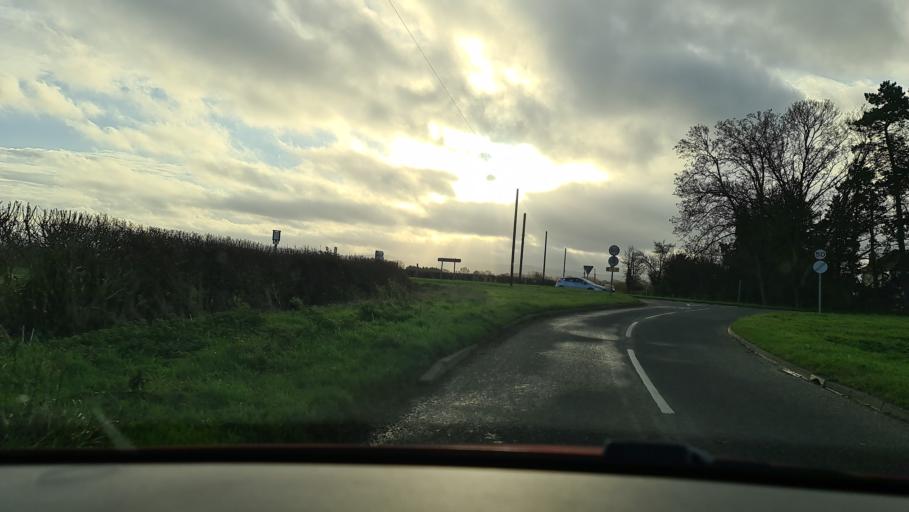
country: GB
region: England
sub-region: Buckinghamshire
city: Stone
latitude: 51.7838
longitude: -0.8819
